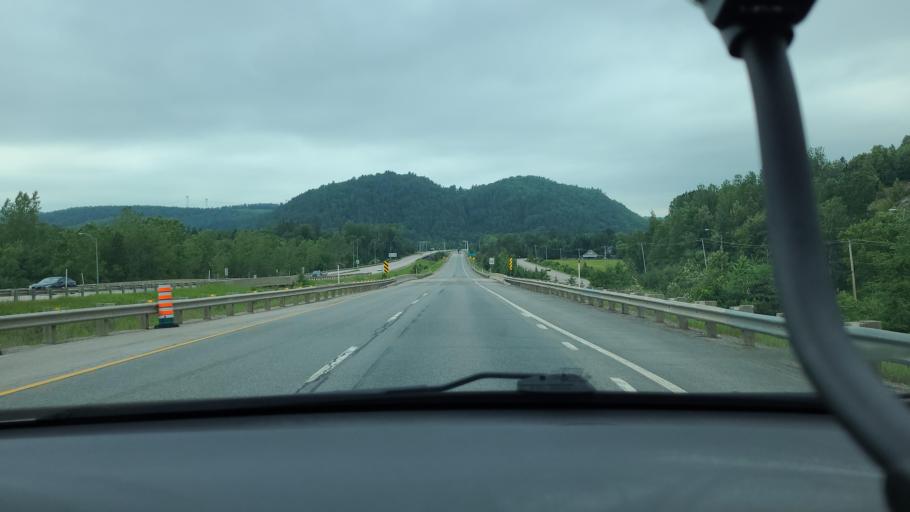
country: CA
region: Quebec
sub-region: Laurentides
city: Mont-Tremblant
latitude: 46.1572
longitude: -74.6889
